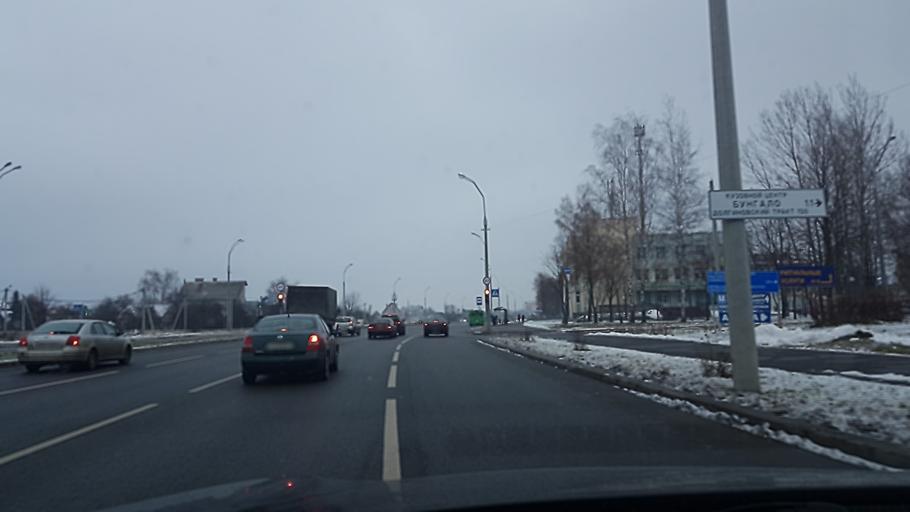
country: BY
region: Minsk
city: Bal'shavik
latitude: 53.9522
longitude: 27.5352
